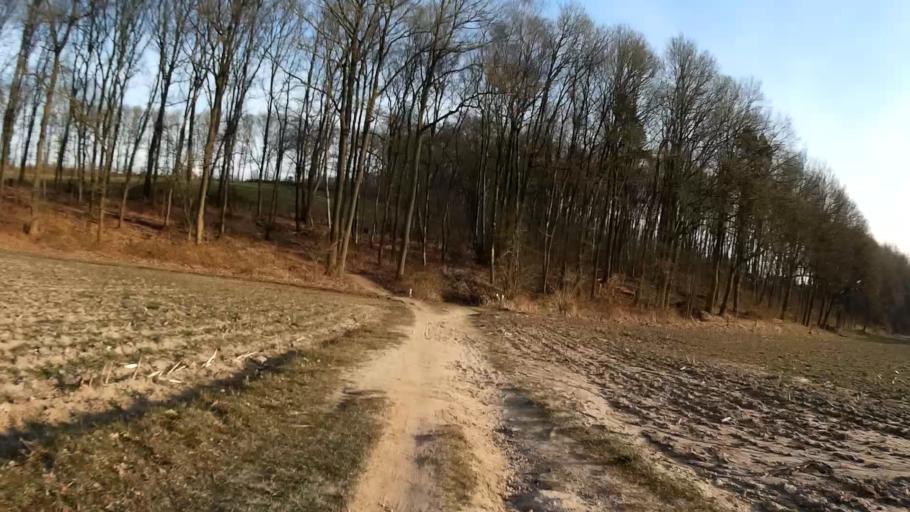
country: NL
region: Utrecht
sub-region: Gemeente Rhenen
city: Rhenen
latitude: 51.9668
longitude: 5.5584
